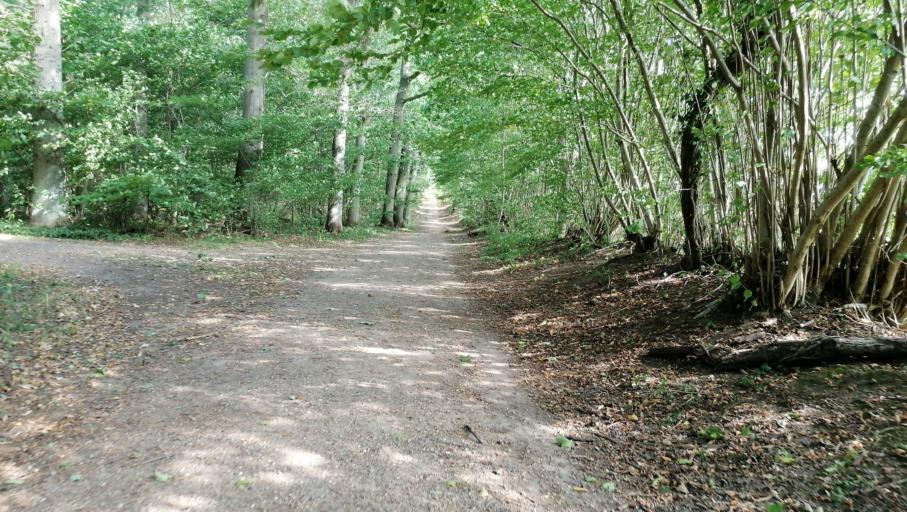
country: DK
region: Zealand
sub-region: Holbaek Kommune
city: Holbaek
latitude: 55.7091
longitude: 11.6909
